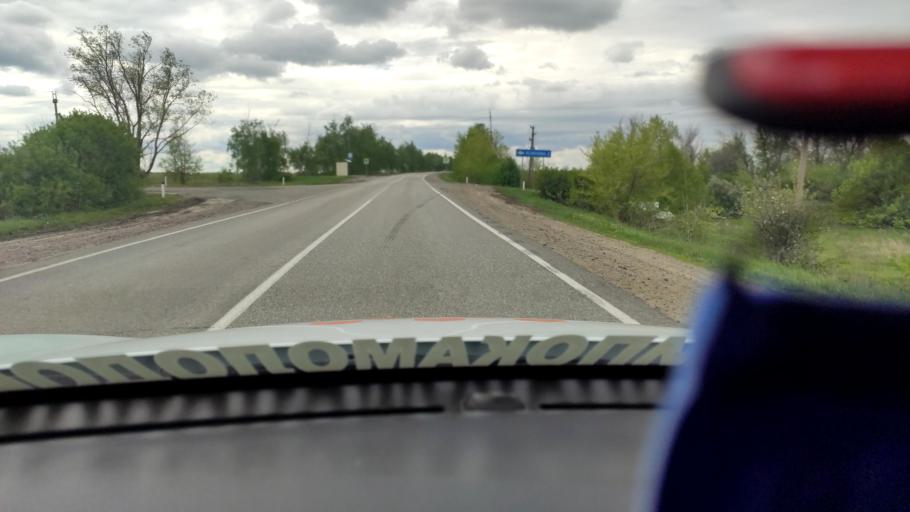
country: RU
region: Voronezj
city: Imeni Pervogo Maya
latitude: 50.7836
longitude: 39.3808
